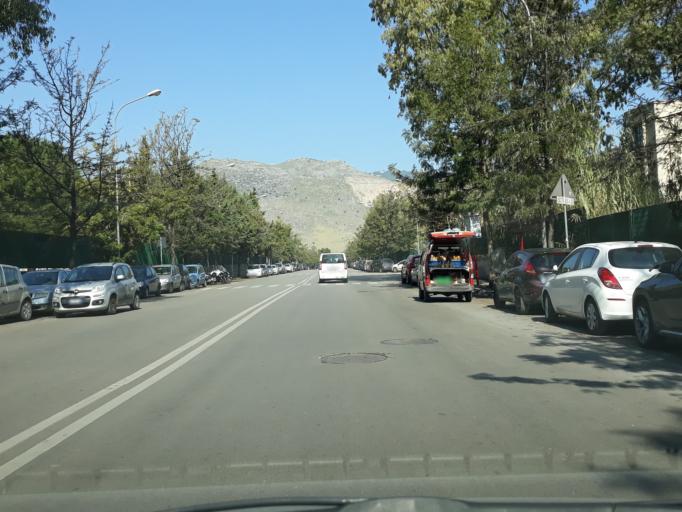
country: IT
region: Sicily
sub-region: Palermo
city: Palermo
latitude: 38.1209
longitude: 13.3059
